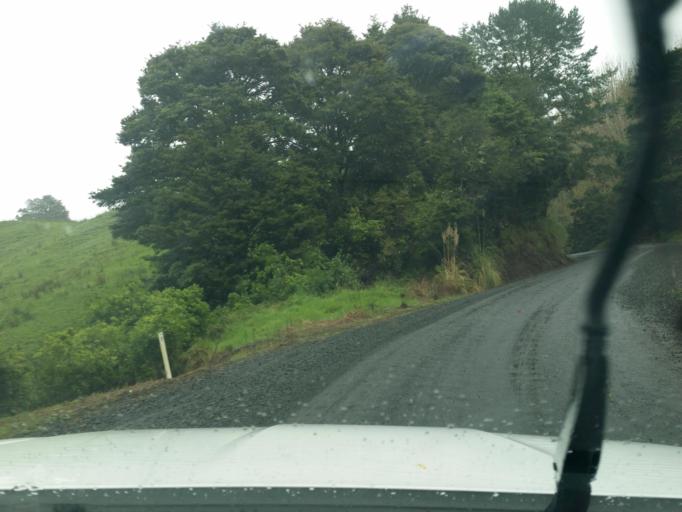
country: NZ
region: Northland
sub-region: Kaipara District
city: Dargaville
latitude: -35.7905
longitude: 173.9717
